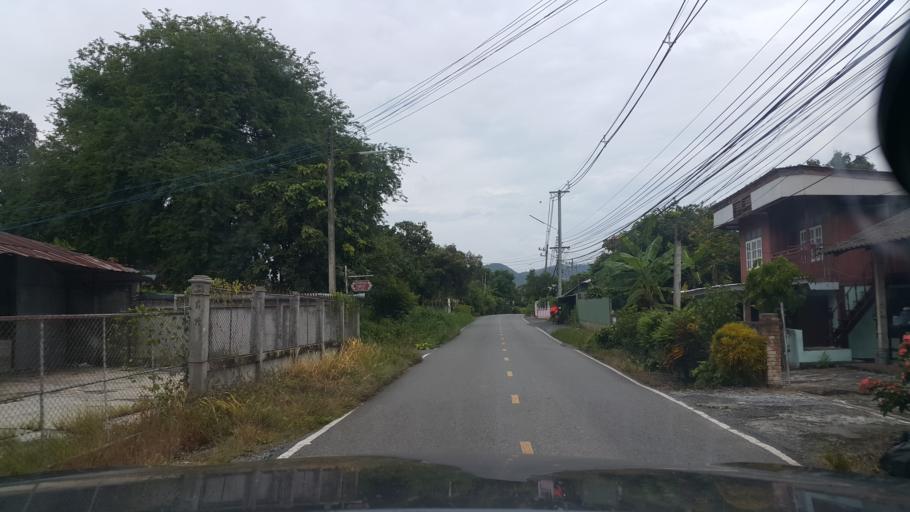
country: TH
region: Chiang Mai
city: San Kamphaeng
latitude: 18.8322
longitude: 99.1651
